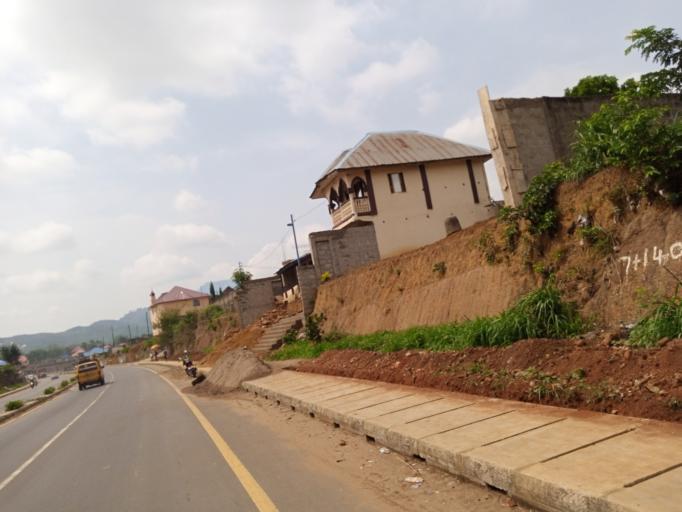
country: SL
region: Western Area
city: Hastings
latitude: 8.3880
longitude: -13.1411
